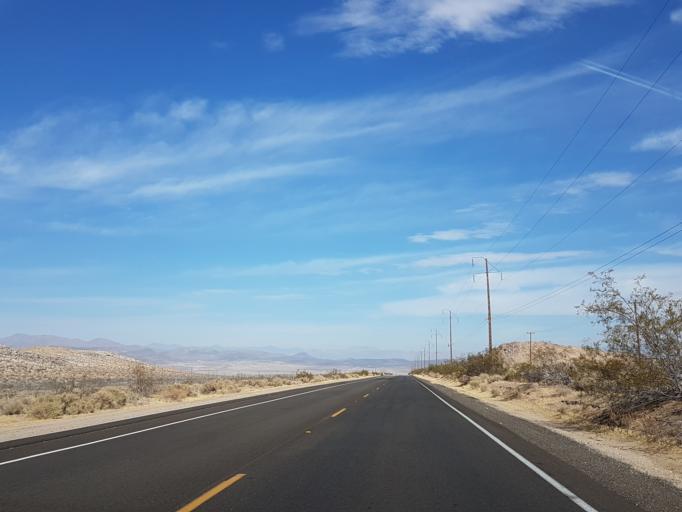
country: US
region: California
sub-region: Kern County
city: Ridgecrest
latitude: 35.6280
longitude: -117.5873
